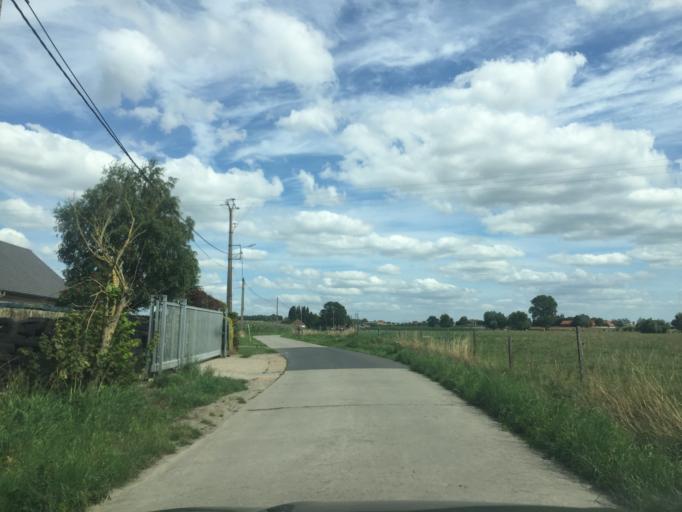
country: BE
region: Flanders
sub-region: Provincie West-Vlaanderen
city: Staden
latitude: 50.9872
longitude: 3.0445
